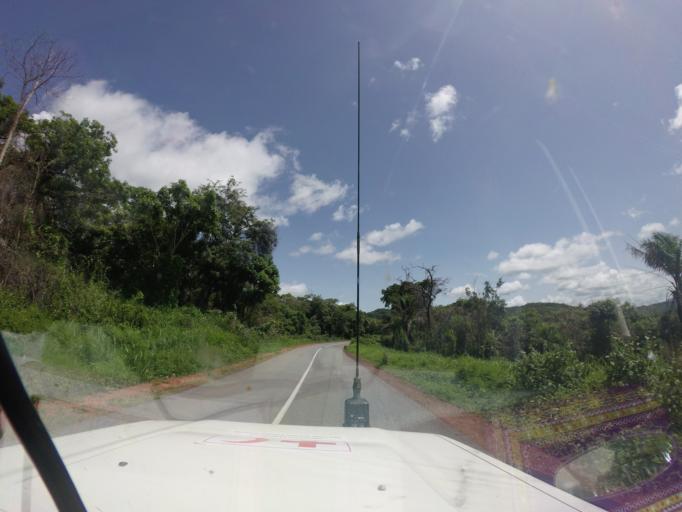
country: GN
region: Mamou
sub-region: Mamou Prefecture
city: Mamou
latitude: 10.1848
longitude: -11.7735
